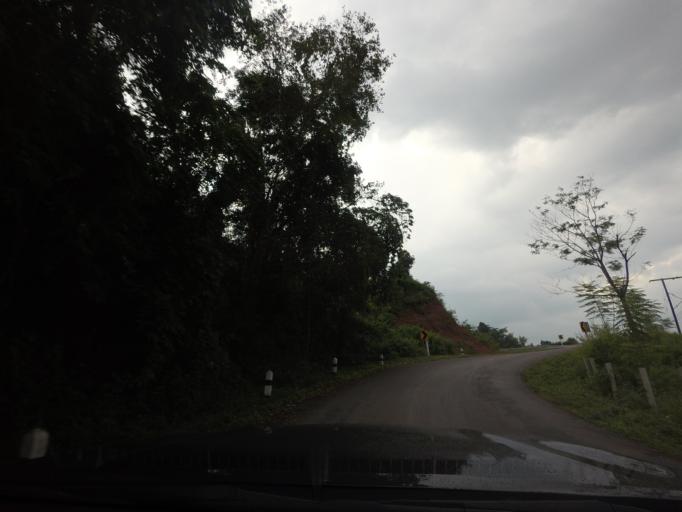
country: TH
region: Nan
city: Bo Kluea
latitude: 19.3461
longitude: 101.1593
